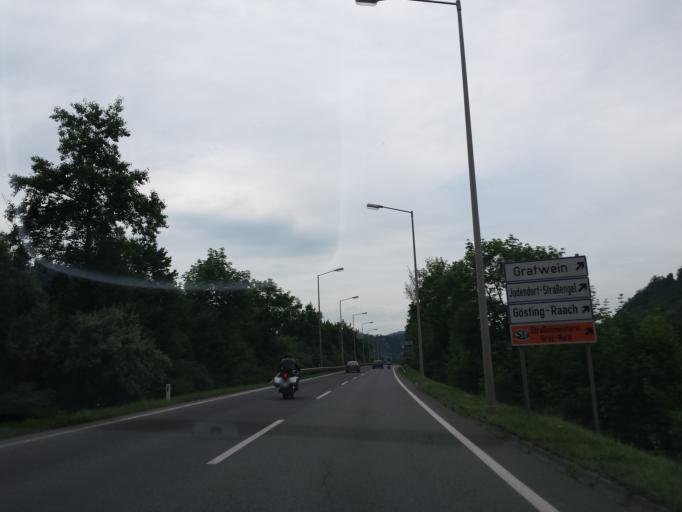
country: AT
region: Styria
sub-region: Graz Stadt
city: Goesting
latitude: 47.1088
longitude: 15.3789
